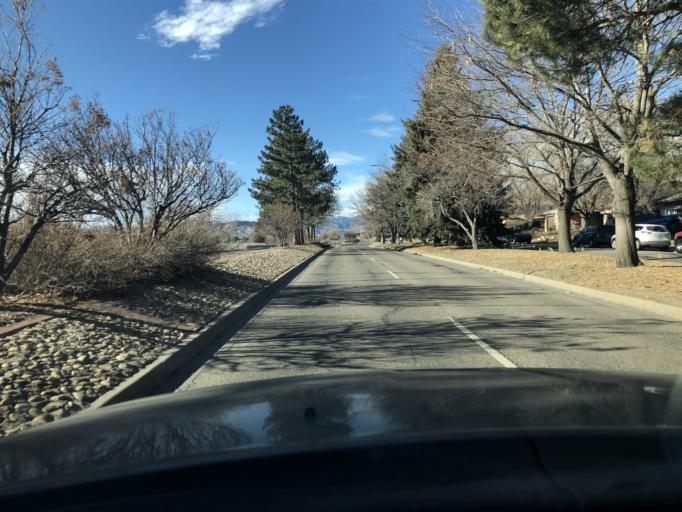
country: US
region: Colorado
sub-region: Jefferson County
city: Arvada
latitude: 39.8019
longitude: -105.1322
